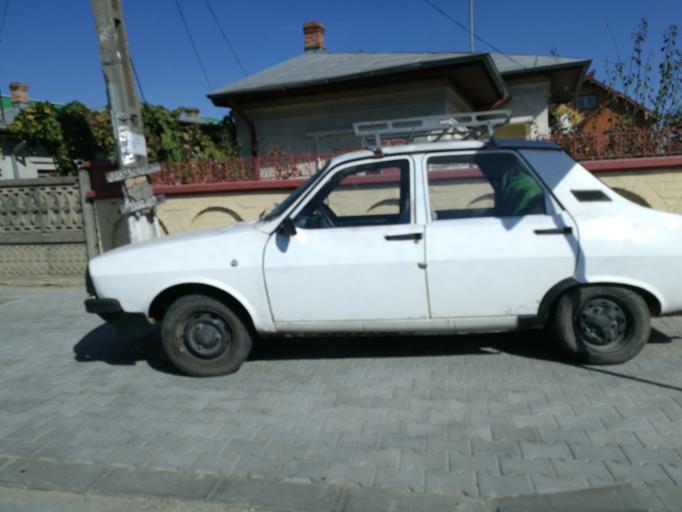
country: RO
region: Ilfov
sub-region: Comuna Dragomiresti-Vale
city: Dragomiresti-Deal
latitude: 44.4611
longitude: 25.9444
